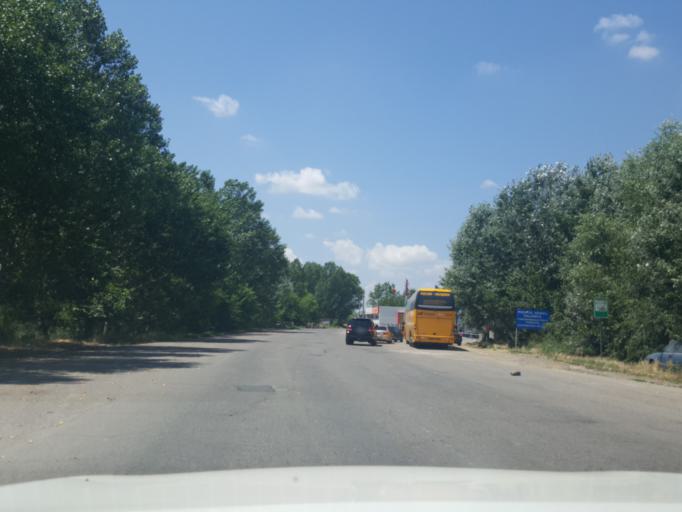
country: UA
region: Odessa
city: Bilyayivka
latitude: 46.4120
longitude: 30.1237
